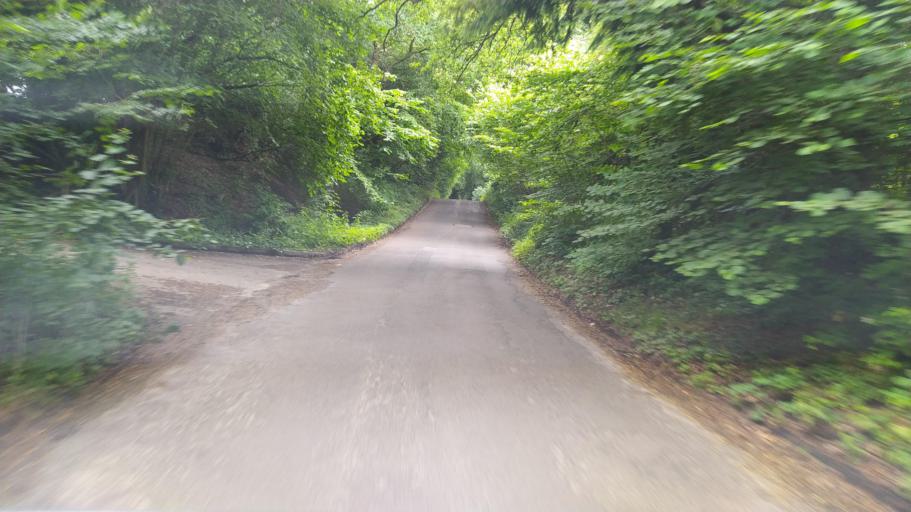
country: GB
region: England
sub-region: Hampshire
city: Liphook
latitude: 51.0878
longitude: -0.8039
